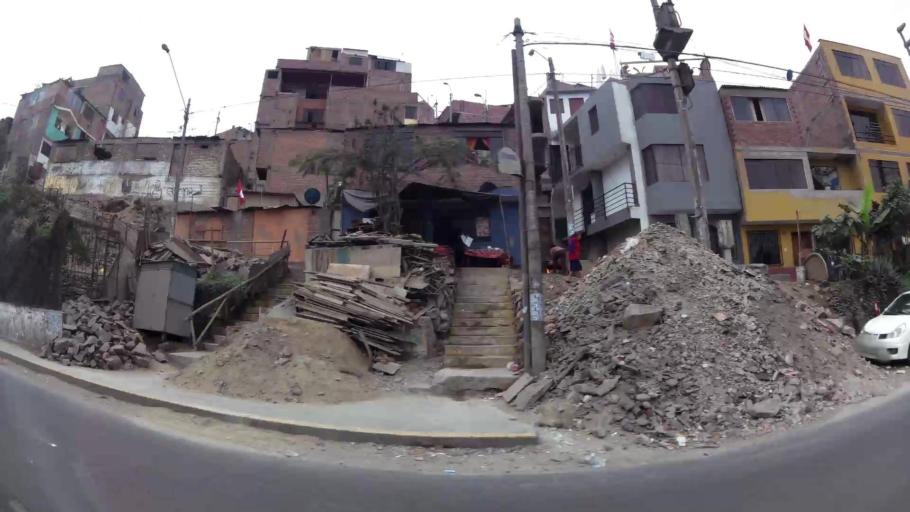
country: PE
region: Lima
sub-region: Lima
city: Surco
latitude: -12.1381
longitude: -76.9750
